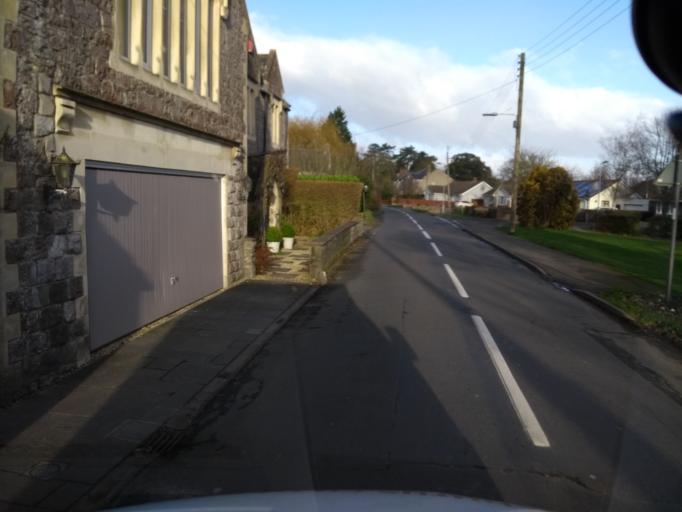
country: GB
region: England
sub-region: North Somerset
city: Bleadon
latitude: 51.2637
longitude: -2.9394
